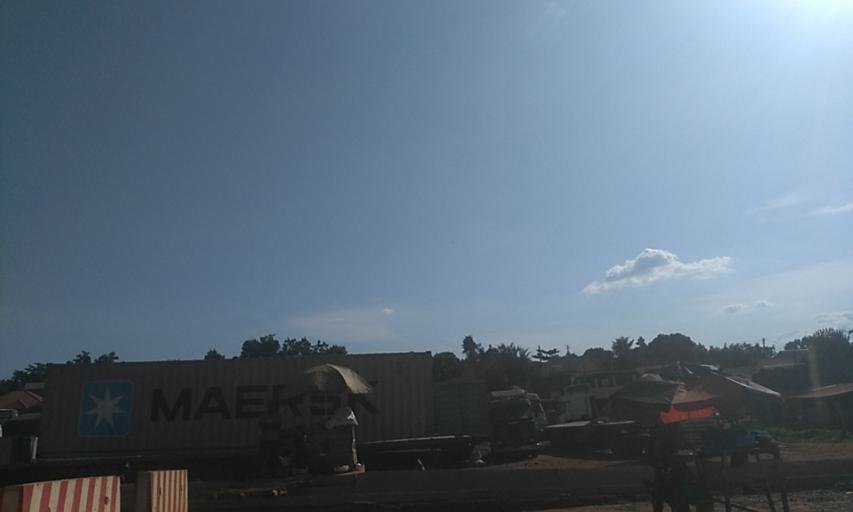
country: UG
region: Central Region
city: Kampala Central Division
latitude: 0.3315
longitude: 32.5283
